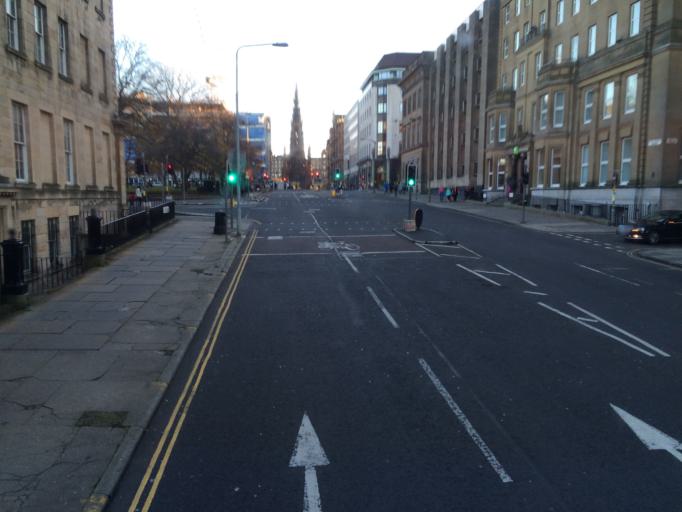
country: GB
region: Scotland
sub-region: Edinburgh
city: Edinburgh
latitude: 55.9549
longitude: -3.1945
